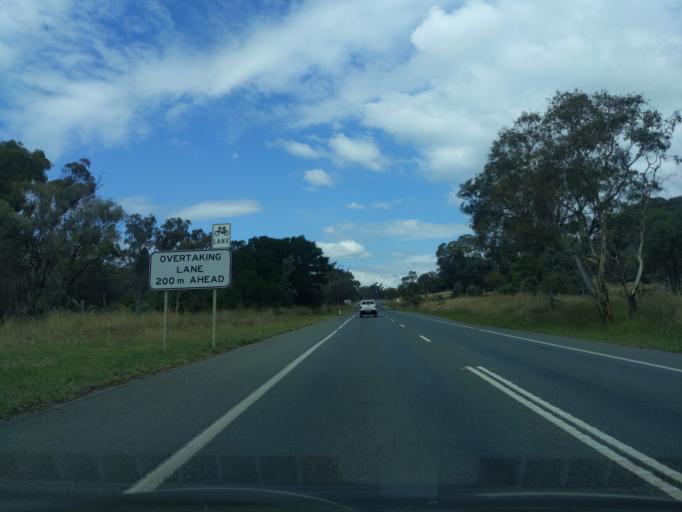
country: AU
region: New South Wales
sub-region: Queanbeyan
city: Queanbeyan
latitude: -35.3202
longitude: 149.2105
